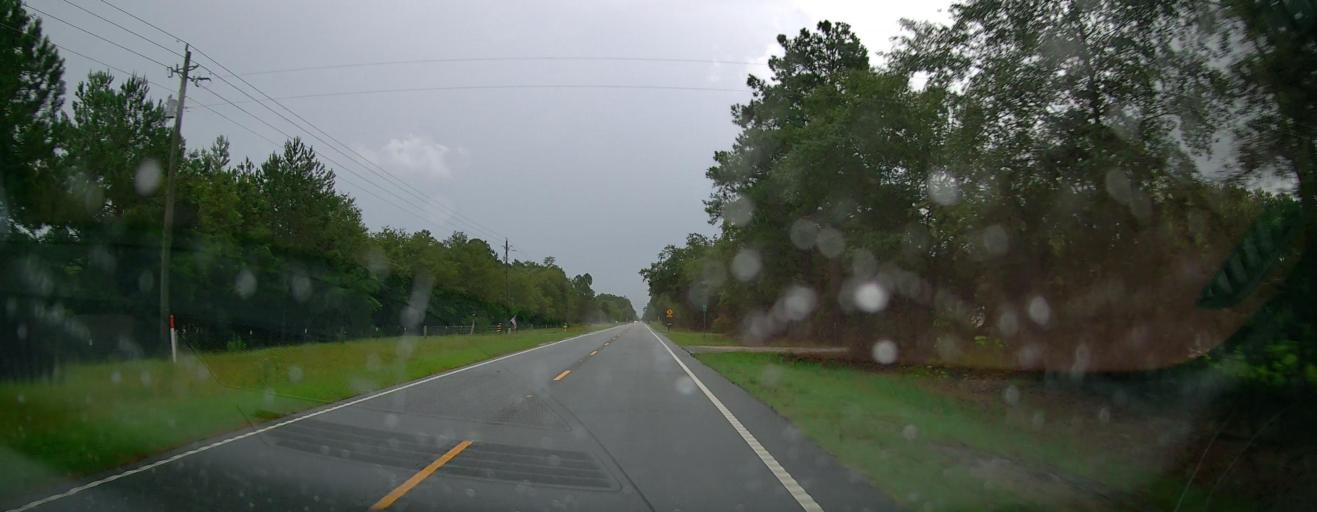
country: US
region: Georgia
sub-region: Brantley County
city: Nahunta
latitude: 31.3418
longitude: -81.9855
